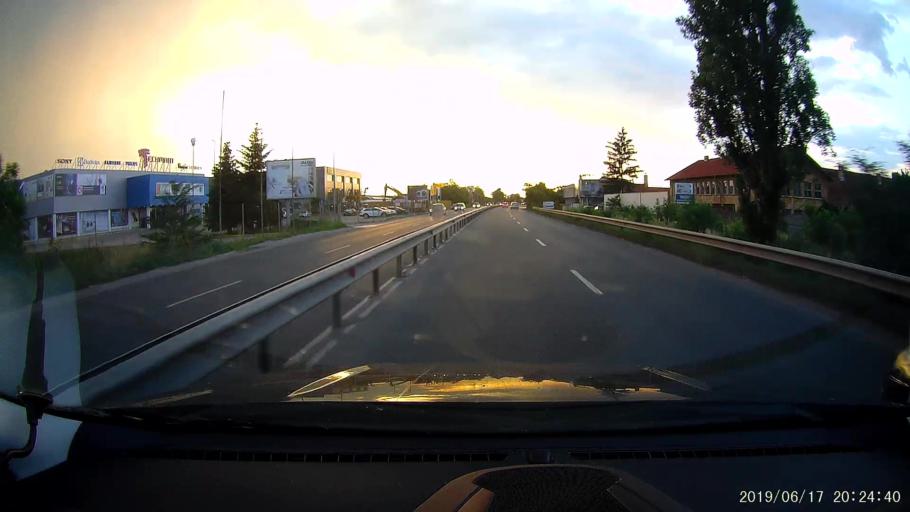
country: BG
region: Sofiya
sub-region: Obshtina Bozhurishte
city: Bozhurishte
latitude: 42.7429
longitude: 23.2330
